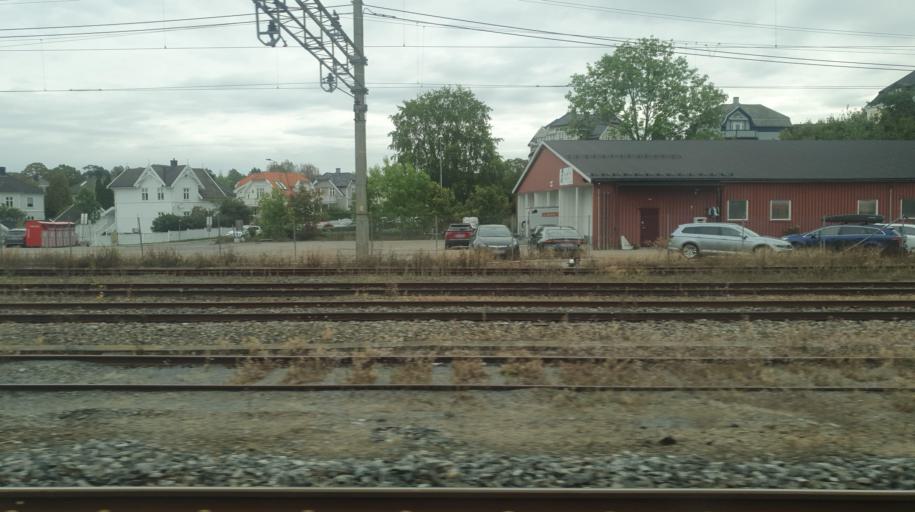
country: NO
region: Vestfold
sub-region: Tonsberg
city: Tonsberg
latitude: 59.2737
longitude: 10.4077
